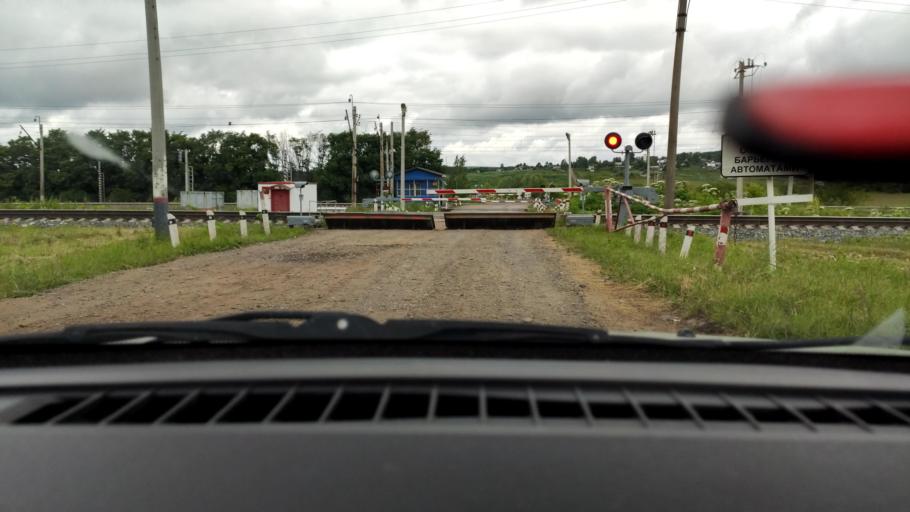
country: RU
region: Perm
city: Chaykovskaya
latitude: 58.1334
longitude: 55.5575
